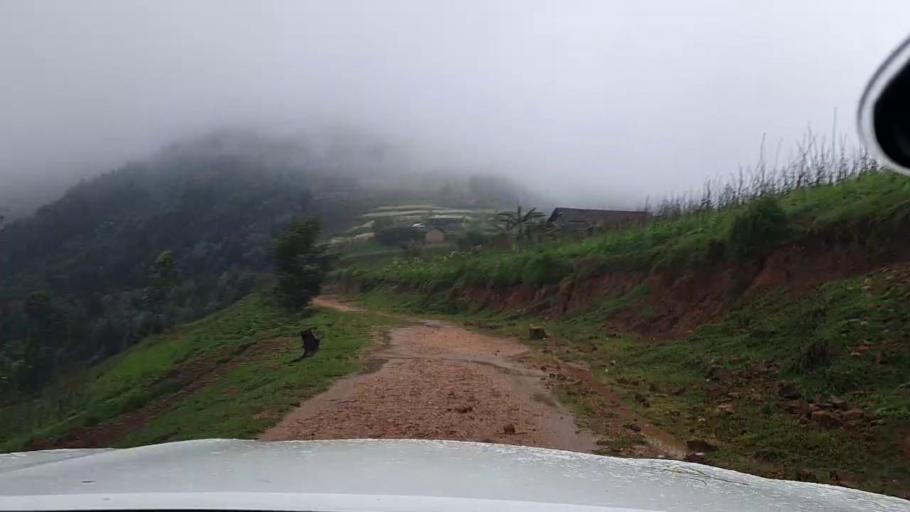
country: RW
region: Western Province
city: Kibuye
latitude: -2.1415
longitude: 29.4605
